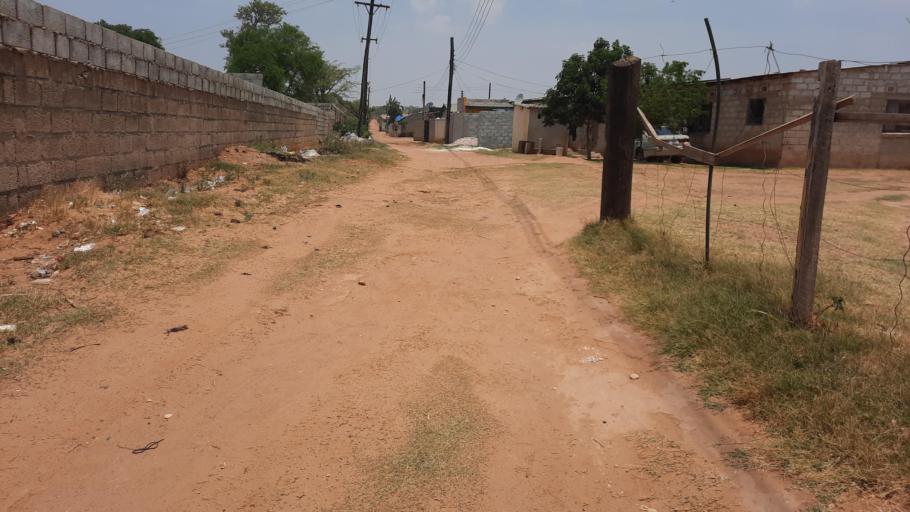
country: ZM
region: Lusaka
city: Lusaka
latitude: -15.4020
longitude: 28.3840
